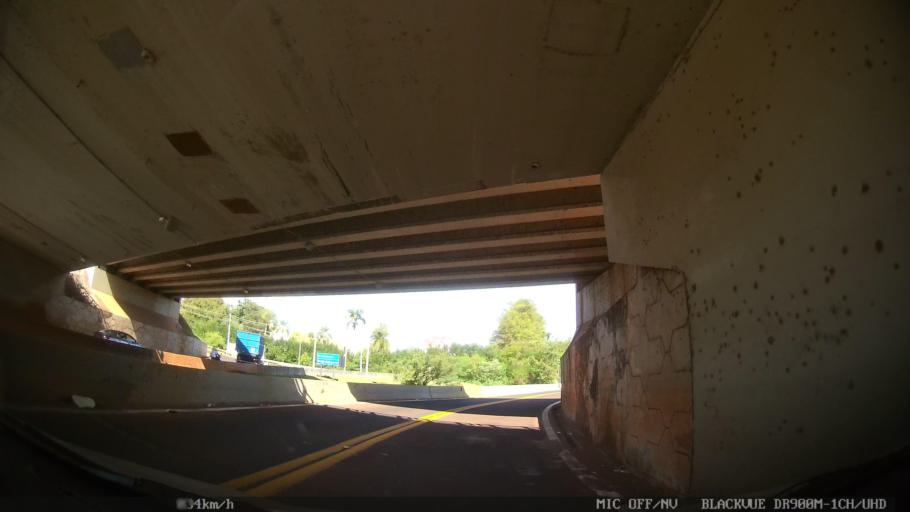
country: BR
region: Sao Paulo
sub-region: Ribeirao Preto
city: Ribeirao Preto
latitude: -21.2160
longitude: -47.8357
